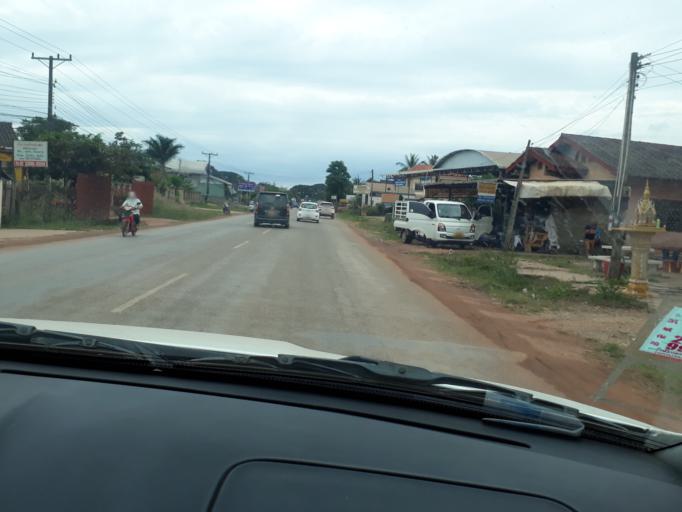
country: LA
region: Vientiane
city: Muang Phon-Hong
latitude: 18.3399
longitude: 102.4335
